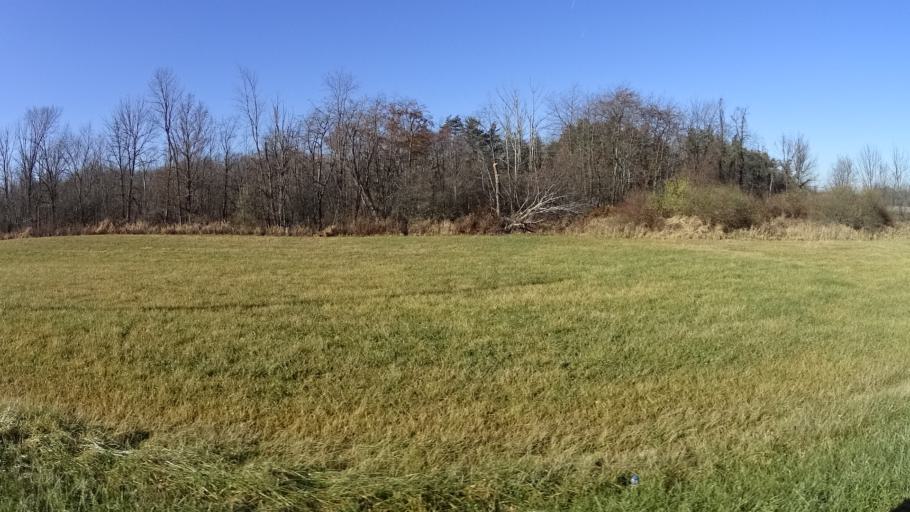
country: US
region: Ohio
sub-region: Lorain County
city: Wellington
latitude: 41.0660
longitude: -82.1815
